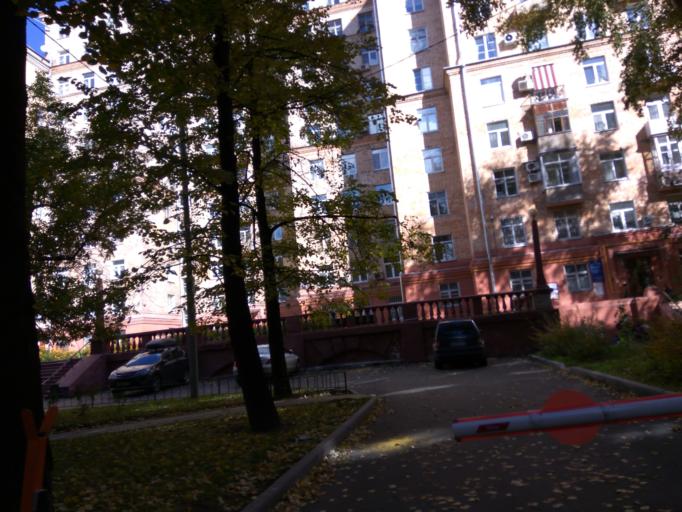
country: RU
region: Moscow
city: Novyye Cheremushki
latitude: 55.7198
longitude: 37.5821
